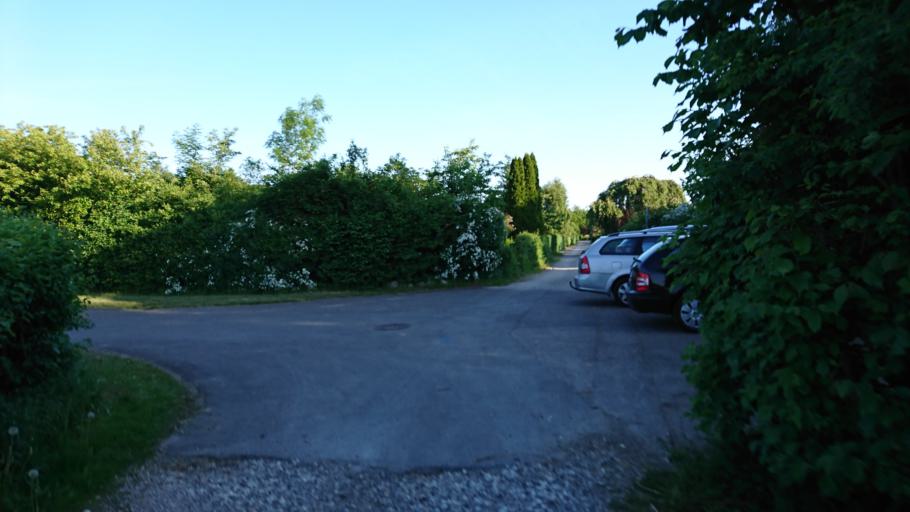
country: DK
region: Capital Region
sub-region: Ballerup Kommune
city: Ballerup
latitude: 55.7175
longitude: 12.3419
